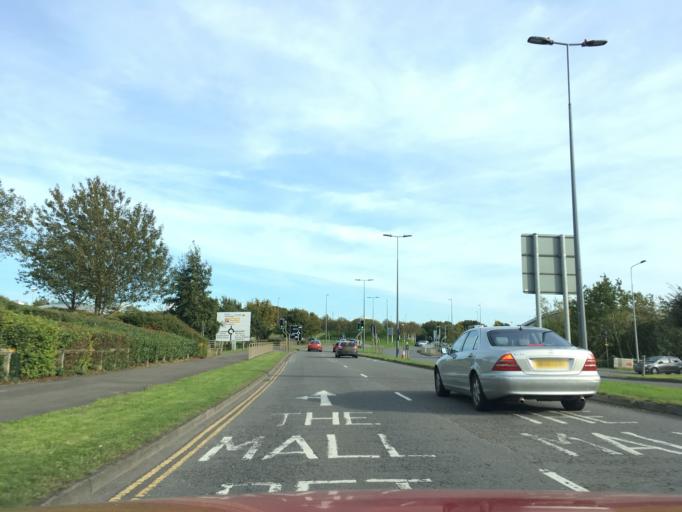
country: GB
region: England
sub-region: South Gloucestershire
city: Almondsbury
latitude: 51.5262
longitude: -2.6064
